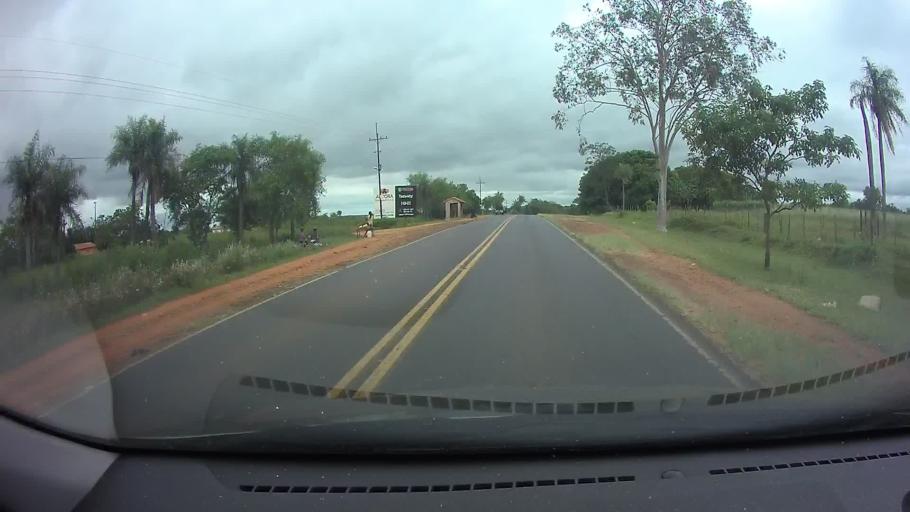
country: PY
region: Central
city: Guarambare
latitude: -25.5242
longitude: -57.4951
